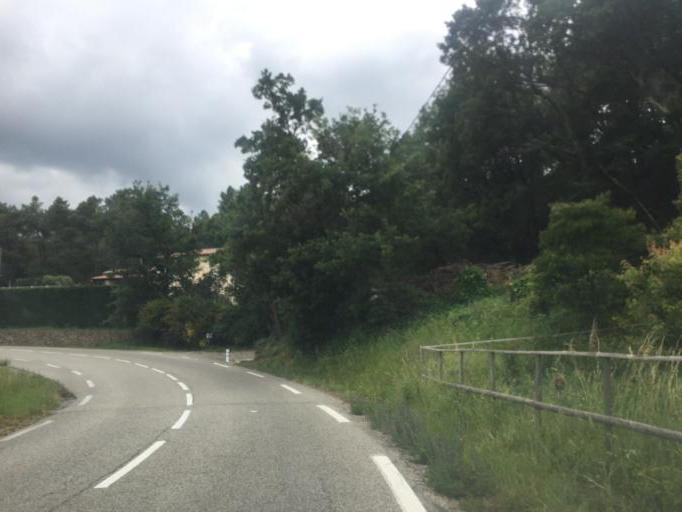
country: FR
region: Rhone-Alpes
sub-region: Departement de l'Ardeche
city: Coux
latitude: 44.7475
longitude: 4.6094
